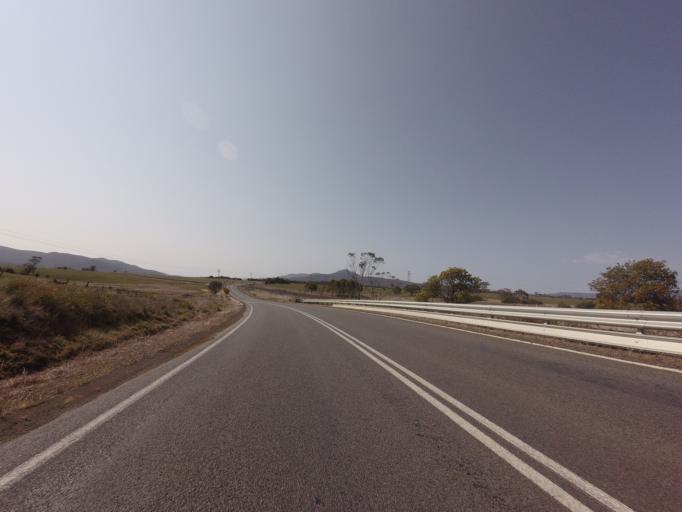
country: AU
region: Tasmania
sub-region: Northern Midlands
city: Evandale
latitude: -41.7988
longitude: 147.7015
